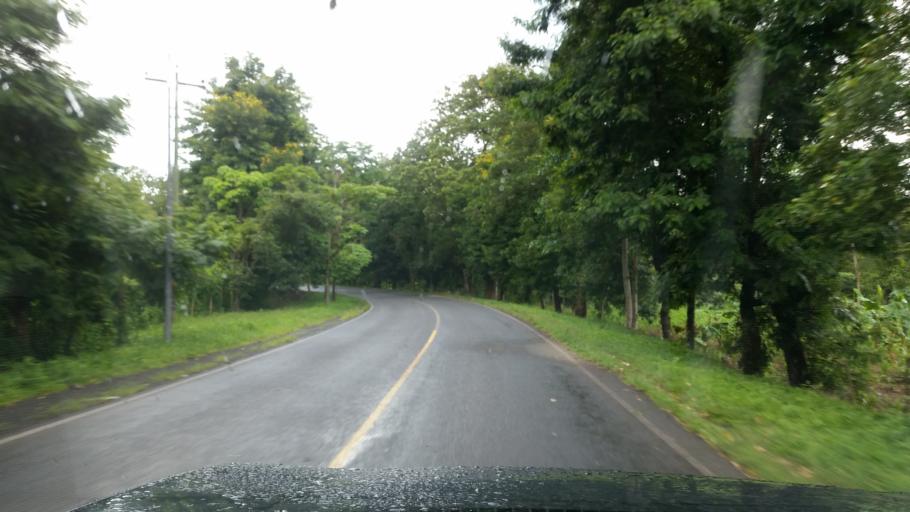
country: NI
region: Matagalpa
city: San Ramon
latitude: 13.0466
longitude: -85.7680
